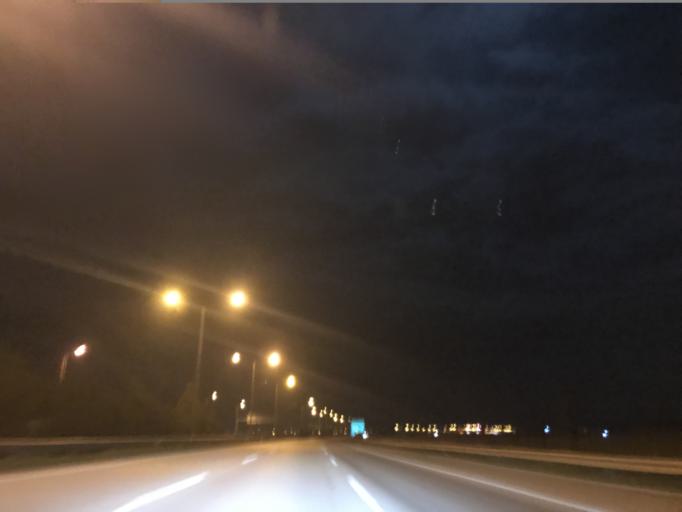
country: TR
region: Hatay
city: Mahmutlar
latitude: 36.9582
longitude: 36.1415
